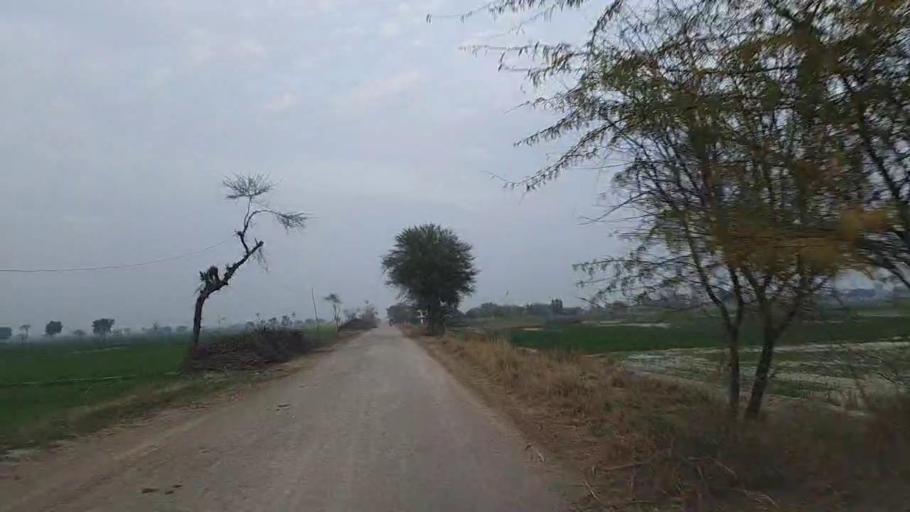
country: PK
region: Sindh
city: Jam Sahib
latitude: 26.3035
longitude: 68.5936
